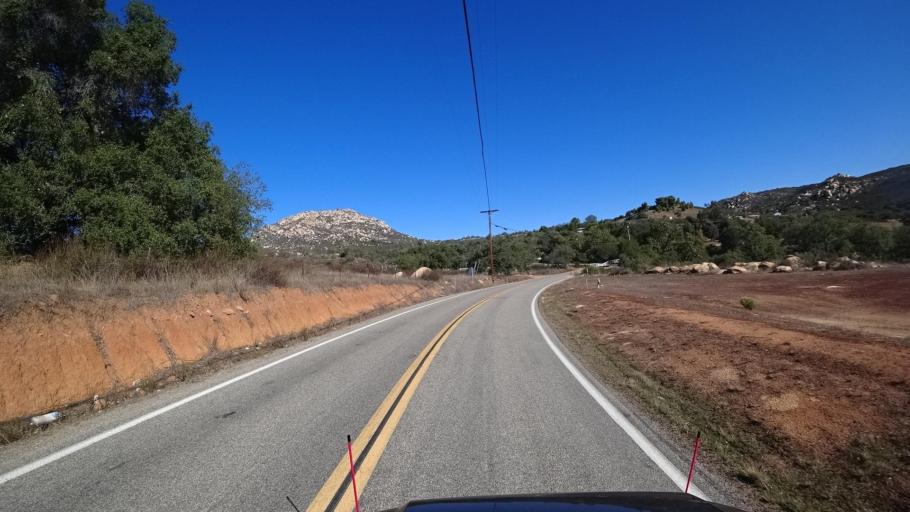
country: US
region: California
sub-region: San Diego County
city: Jamul
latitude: 32.6832
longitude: -116.7543
